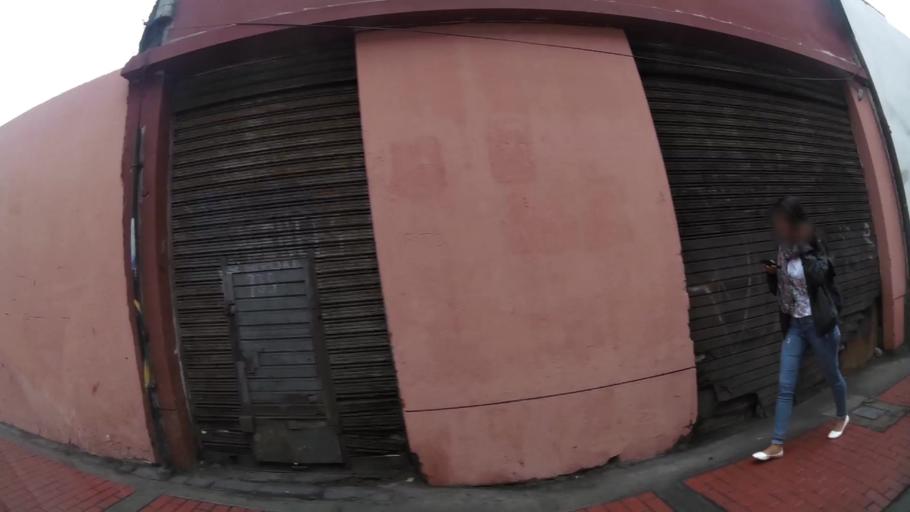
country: PE
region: Lima
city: Lima
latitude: -12.0485
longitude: -77.0374
